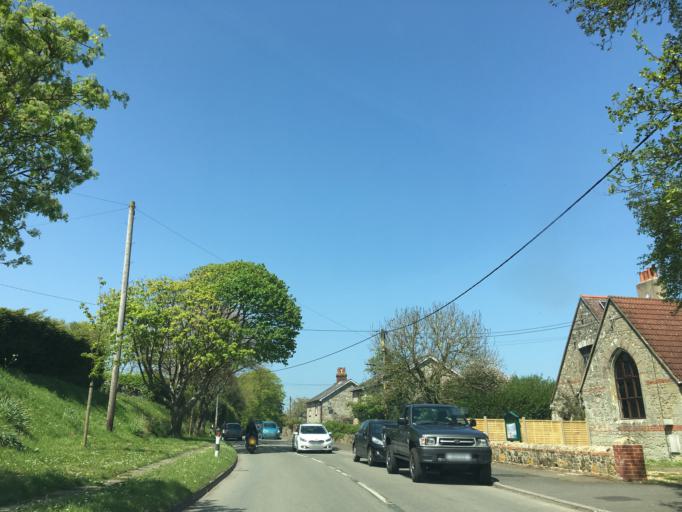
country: GB
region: England
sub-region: Isle of Wight
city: Niton
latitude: 50.5955
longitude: -1.2628
